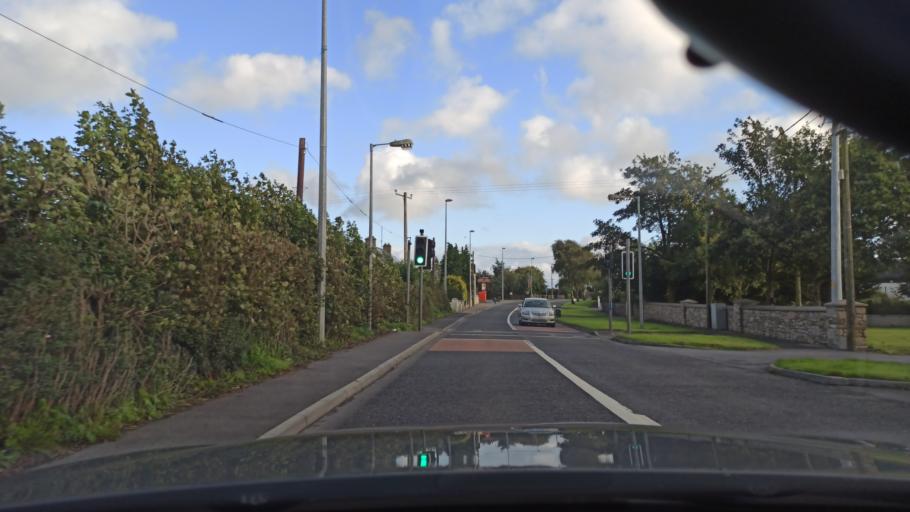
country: IE
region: Munster
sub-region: North Tipperary
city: Roscrea
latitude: 52.9410
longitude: -7.7890
